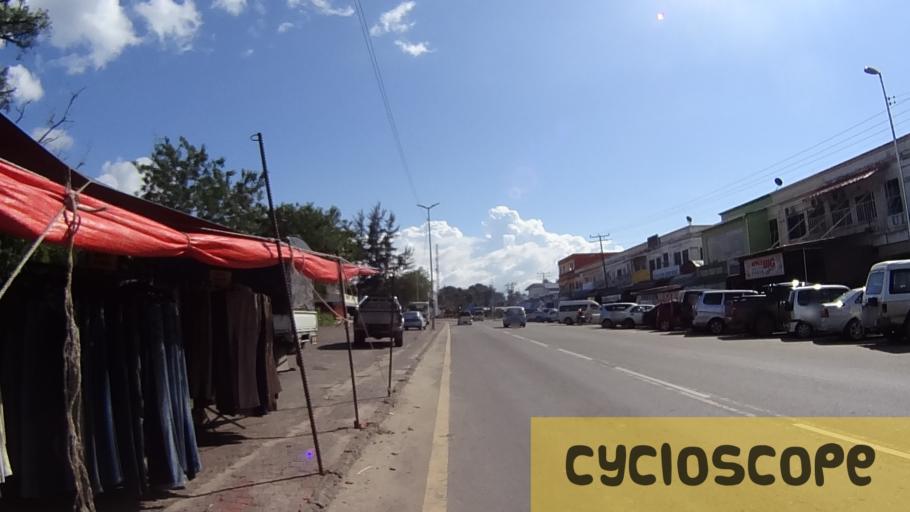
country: MY
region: Sabah
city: Beaufort
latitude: 5.0758
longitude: 115.5492
